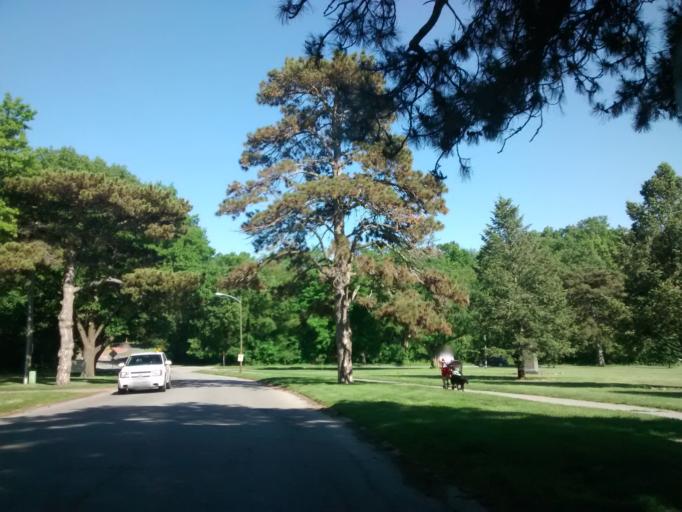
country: US
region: Nebraska
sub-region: Douglas County
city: Ralston
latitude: 41.2547
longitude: -96.0061
